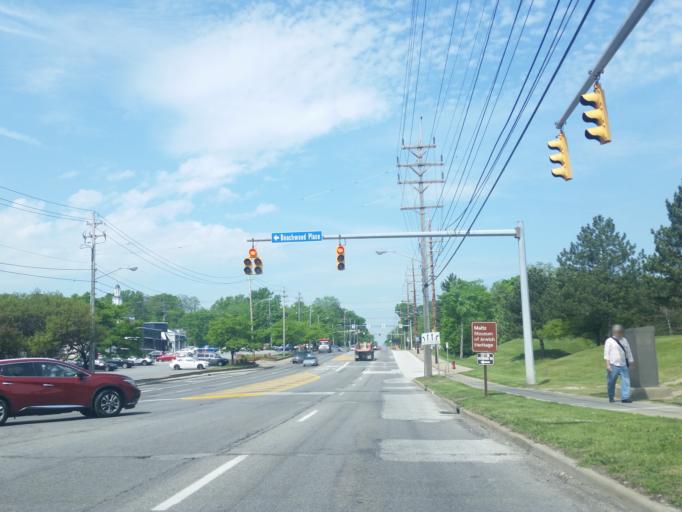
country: US
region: Ohio
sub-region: Cuyahoga County
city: Lyndhurst
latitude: 41.5013
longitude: -81.4947
